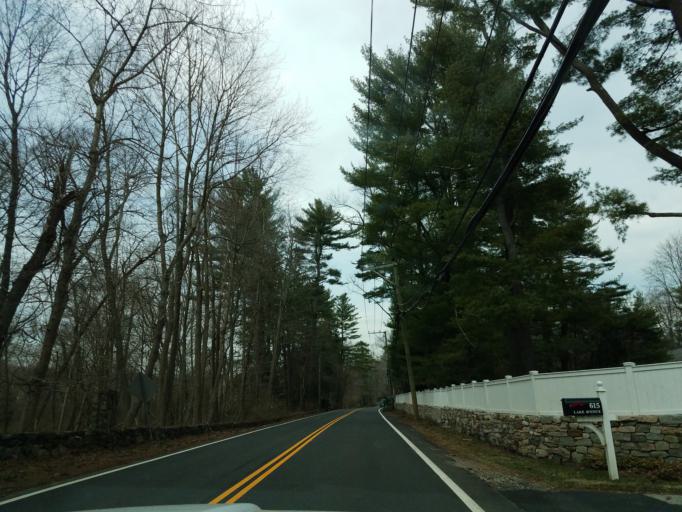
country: US
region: Connecticut
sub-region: Fairfield County
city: Glenville
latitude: 41.0670
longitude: -73.6394
